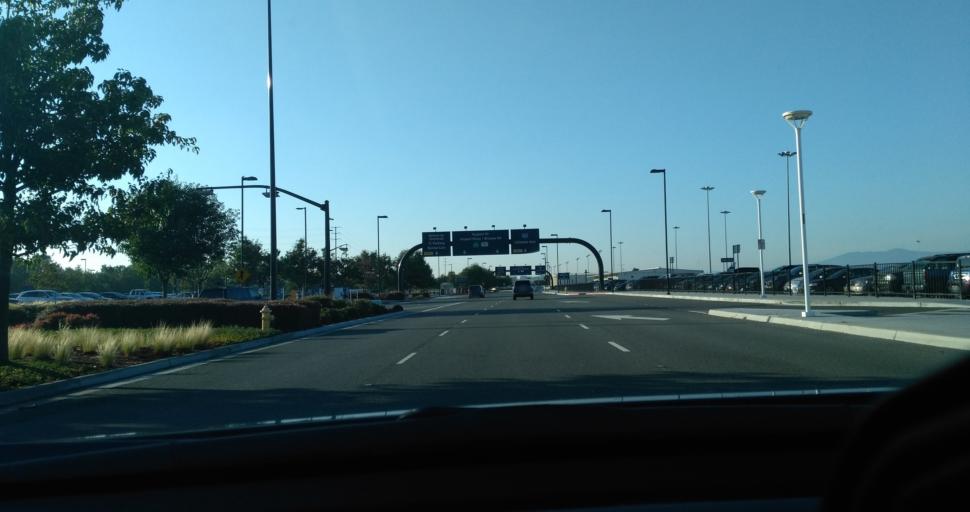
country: US
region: California
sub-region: Santa Clara County
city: San Jose
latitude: 37.3626
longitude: -121.9211
